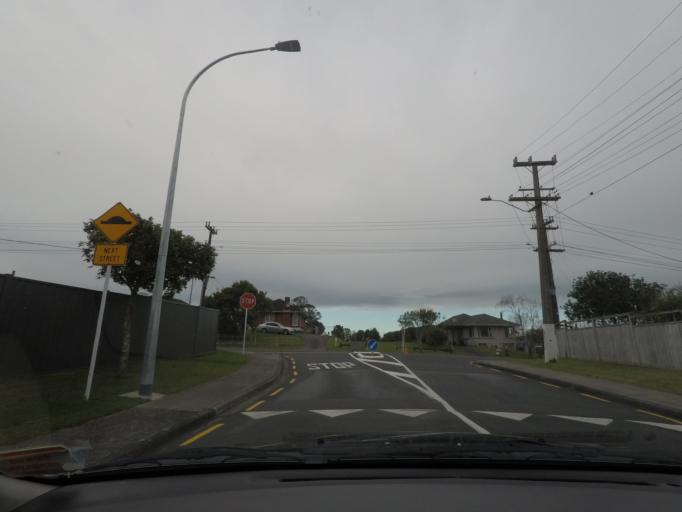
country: NZ
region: Auckland
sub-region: Auckland
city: Rosebank
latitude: -36.8633
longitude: 174.6409
